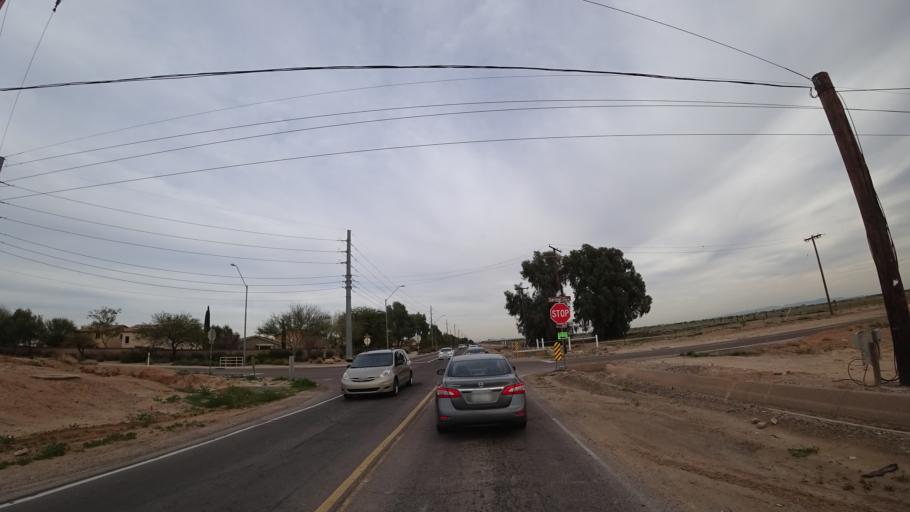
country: US
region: Arizona
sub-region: Maricopa County
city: Citrus Park
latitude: 33.6097
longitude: -112.4098
